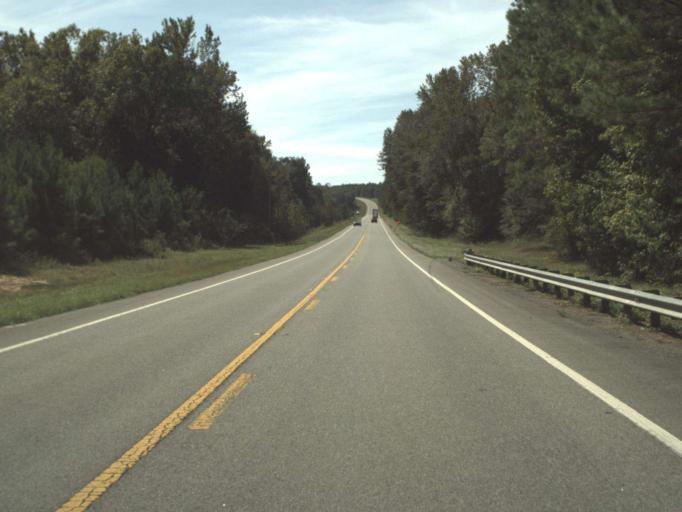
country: US
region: Florida
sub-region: Washington County
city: Chipley
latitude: 30.5625
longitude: -85.6157
